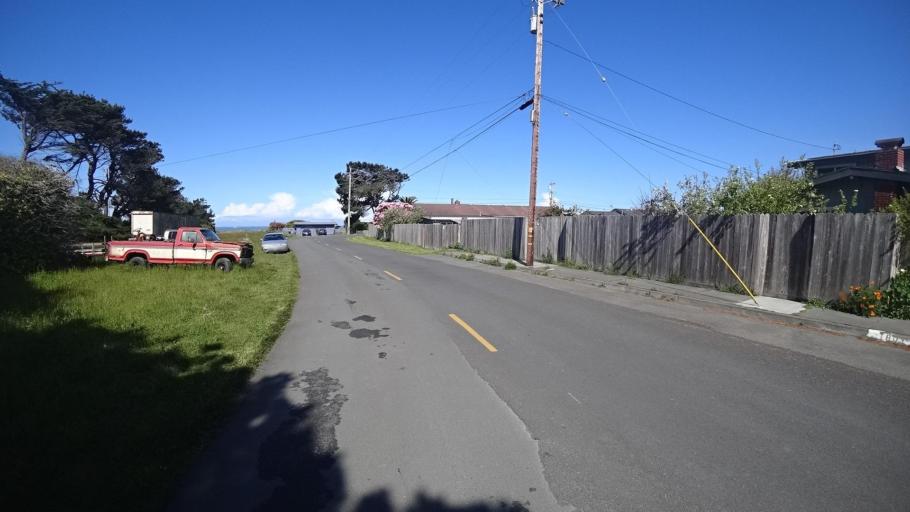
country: US
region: California
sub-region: Humboldt County
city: McKinleyville
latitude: 40.9380
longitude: -124.1267
